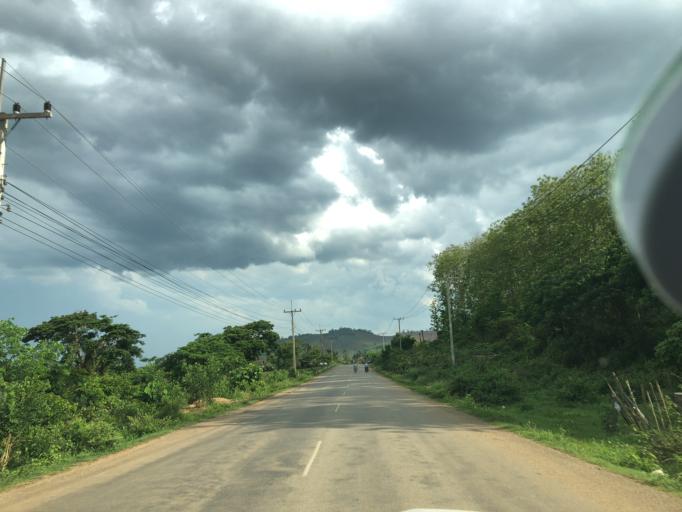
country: TH
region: Uttaradit
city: Ban Khok
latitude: 18.1445
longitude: 101.3820
